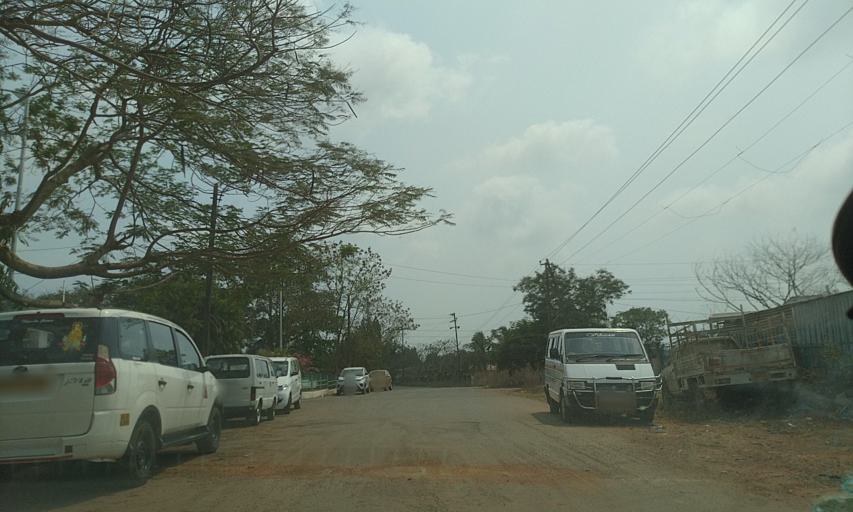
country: IN
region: Goa
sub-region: South Goa
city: Sancoale
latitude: 15.3757
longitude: 73.9279
